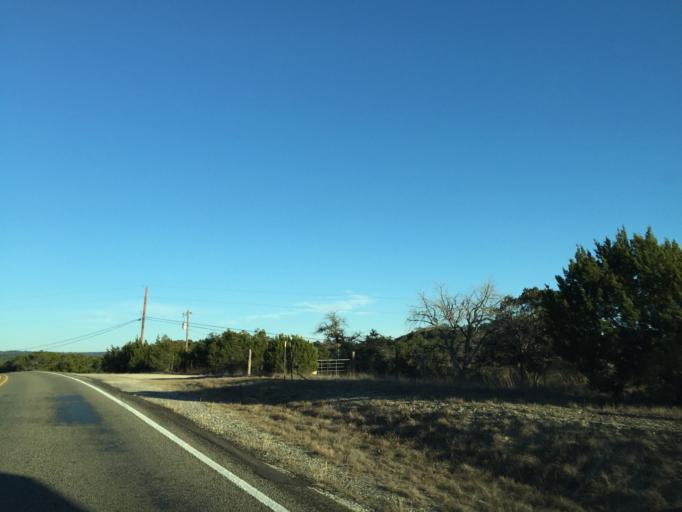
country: US
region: Texas
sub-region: Travis County
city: Lago Vista
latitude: 30.5204
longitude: -98.0617
